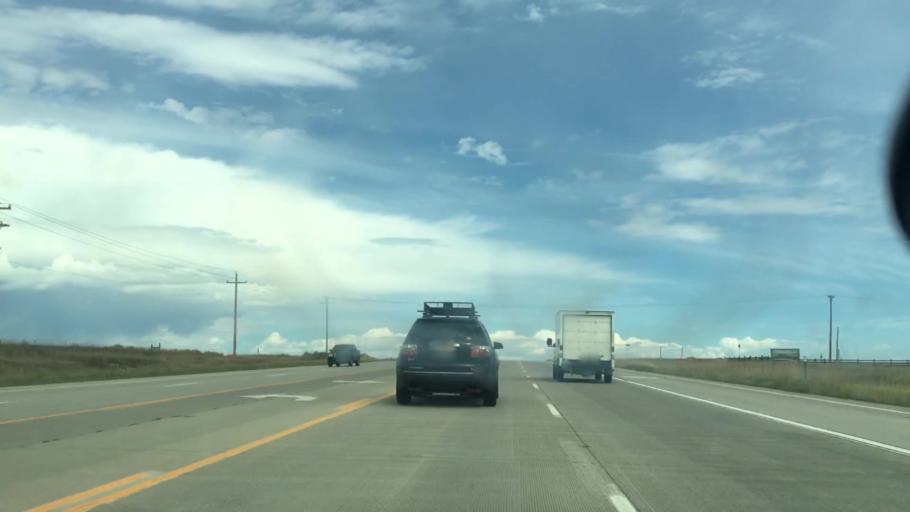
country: US
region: Colorado
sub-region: Larimer County
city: Berthoud
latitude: 40.2821
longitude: -105.1025
